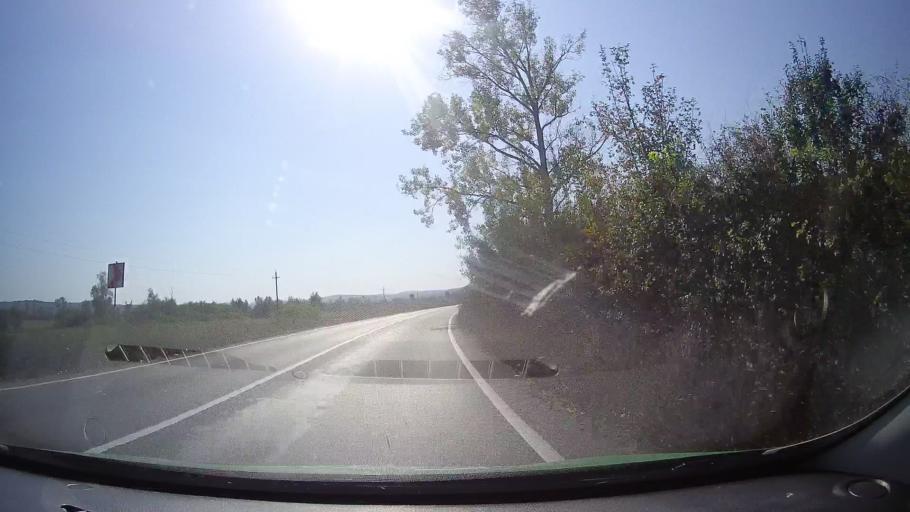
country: RO
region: Arad
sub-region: Comuna Ususau
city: Ususau
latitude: 46.1007
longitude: 21.8148
